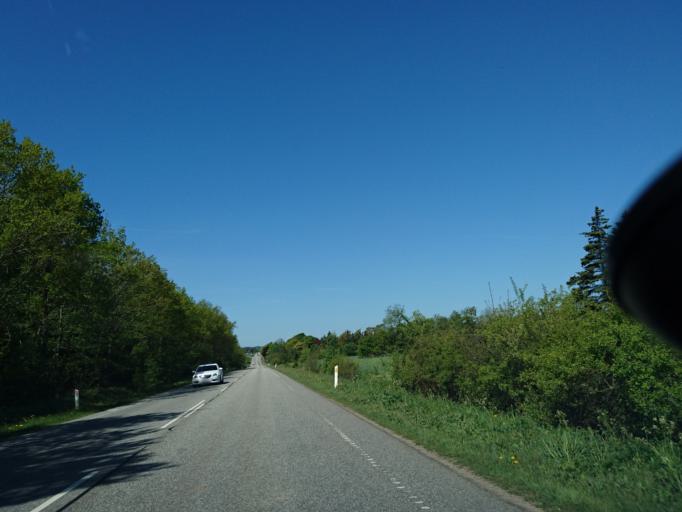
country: DK
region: North Denmark
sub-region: Hjorring Kommune
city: Sindal
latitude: 57.4659
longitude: 10.2702
